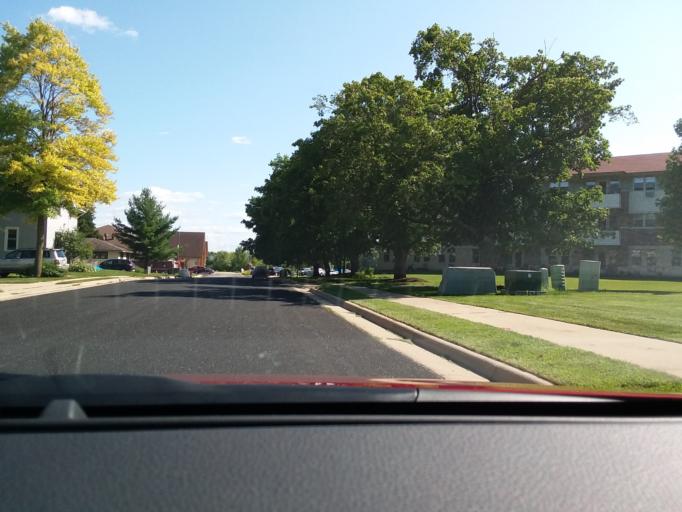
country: US
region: Wisconsin
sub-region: Dane County
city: Waunakee
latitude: 43.1905
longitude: -89.4497
